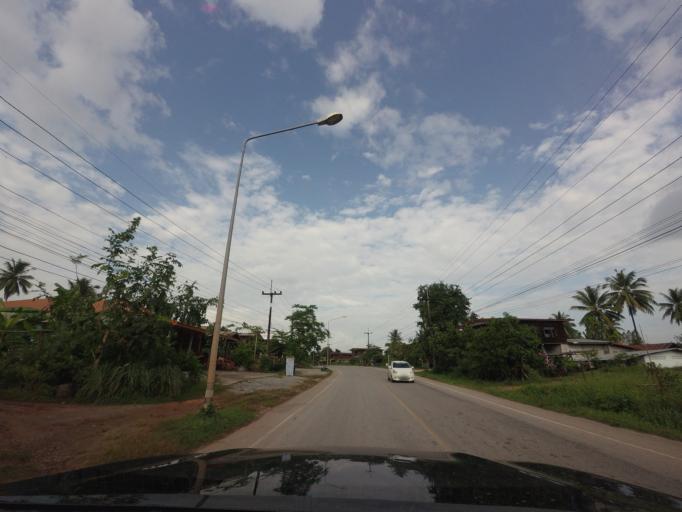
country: TH
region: Nong Khai
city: Pho Tak
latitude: 17.7804
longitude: 102.3865
